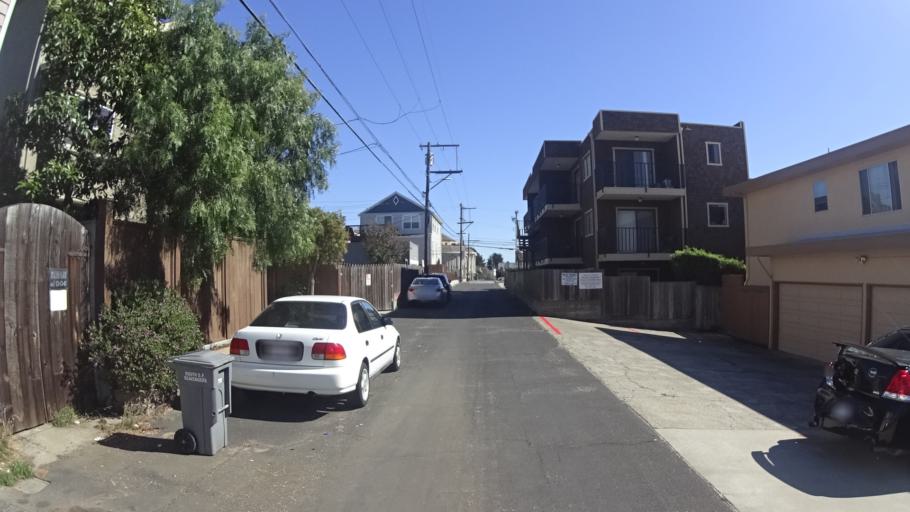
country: US
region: California
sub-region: San Mateo County
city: South San Francisco
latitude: 37.6572
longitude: -122.4168
